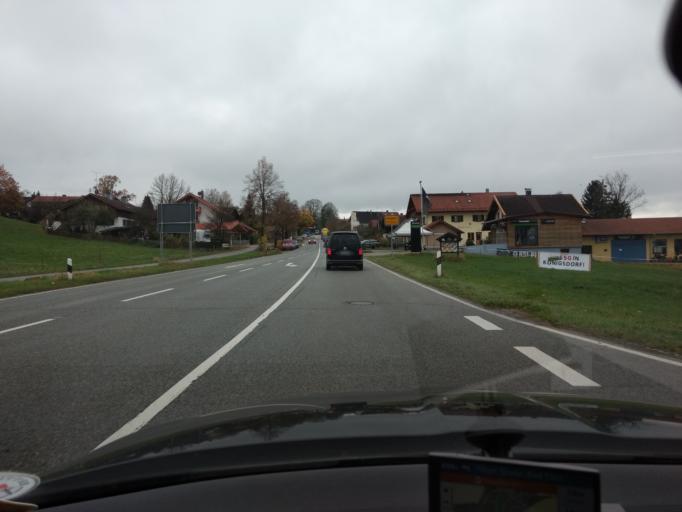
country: DE
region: Bavaria
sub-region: Upper Bavaria
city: Konigsdorf
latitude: 47.8216
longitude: 11.4837
